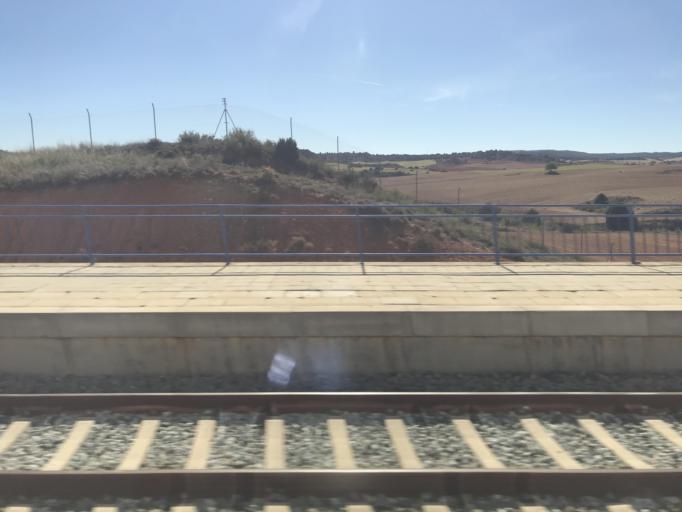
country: ES
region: Aragon
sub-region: Provincia de Zaragoza
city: Cabolafuente
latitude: 41.2258
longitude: -2.0727
